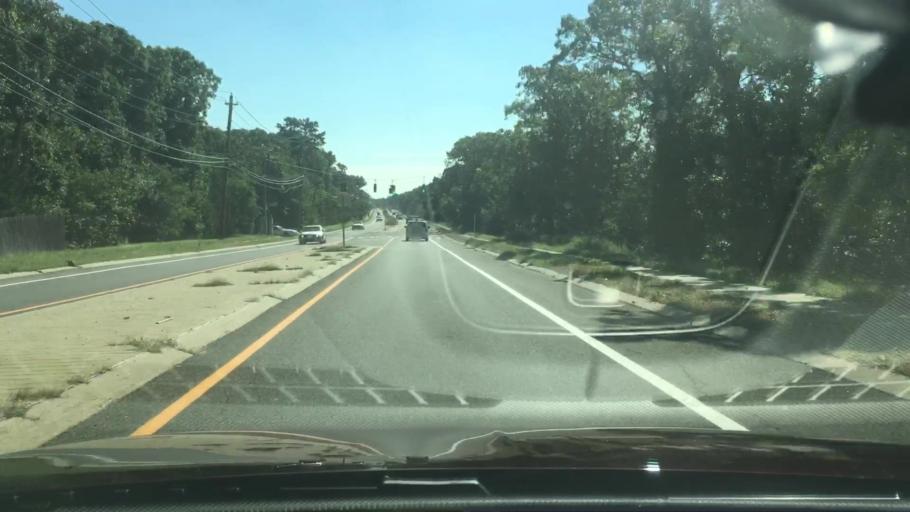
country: US
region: New York
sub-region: Suffolk County
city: Port Jefferson Station
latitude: 40.8999
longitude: -73.0221
